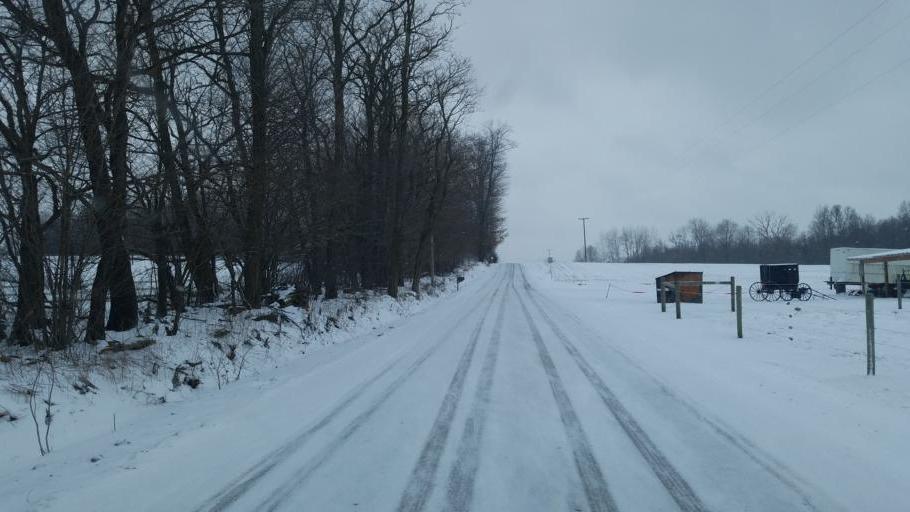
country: US
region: Pennsylvania
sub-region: Crawford County
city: Cochranton
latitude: 41.4309
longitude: -80.0140
